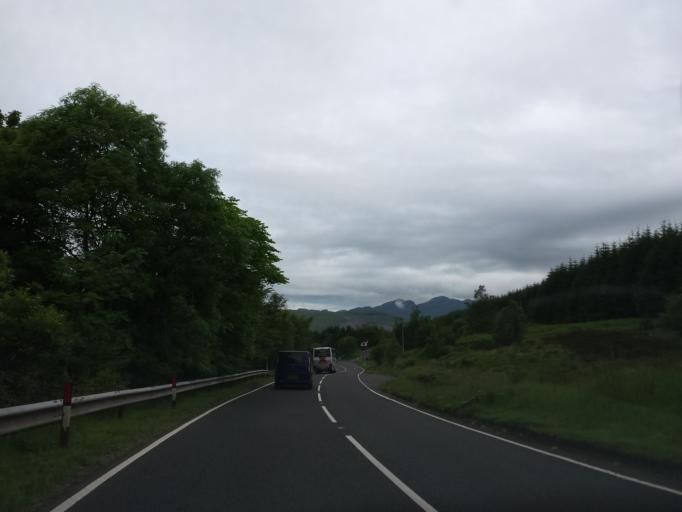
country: GB
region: Scotland
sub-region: Stirling
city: Callander
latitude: 56.4236
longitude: -4.3384
